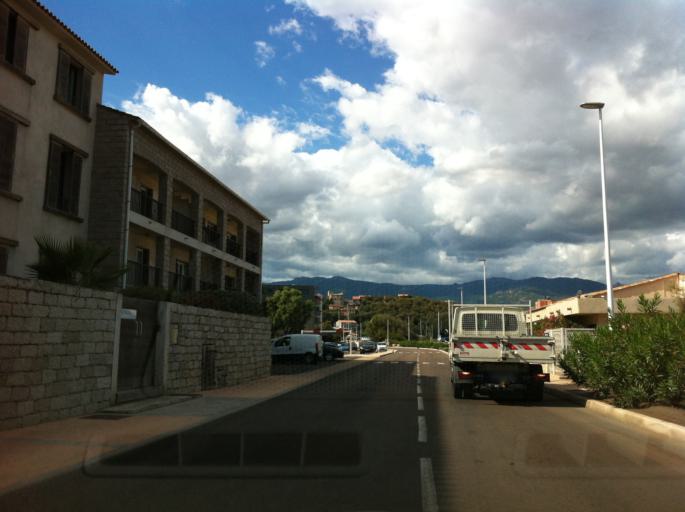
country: FR
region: Corsica
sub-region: Departement de la Corse-du-Sud
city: Porto-Vecchio
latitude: 41.5876
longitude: 9.2890
